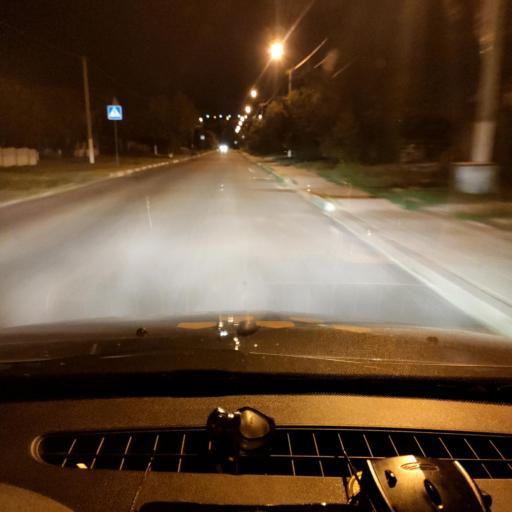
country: RU
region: Belgorod
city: Mayskiy
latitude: 50.5183
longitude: 36.4590
